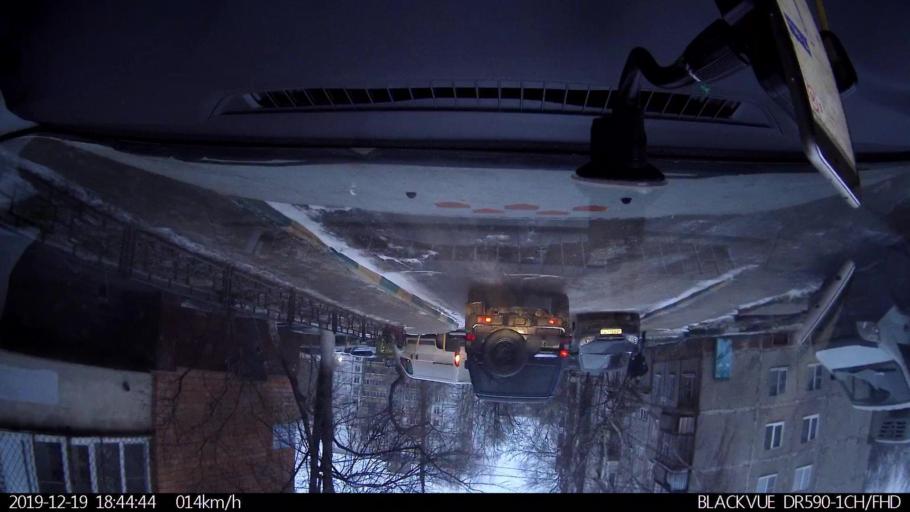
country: RU
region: Nizjnij Novgorod
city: Bor
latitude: 56.3190
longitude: 44.0523
